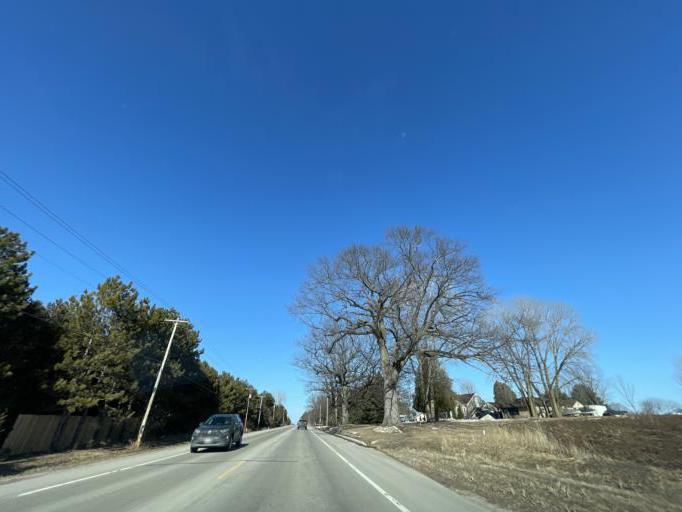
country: US
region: Wisconsin
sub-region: Brown County
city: Suamico
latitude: 44.6097
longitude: -88.0730
